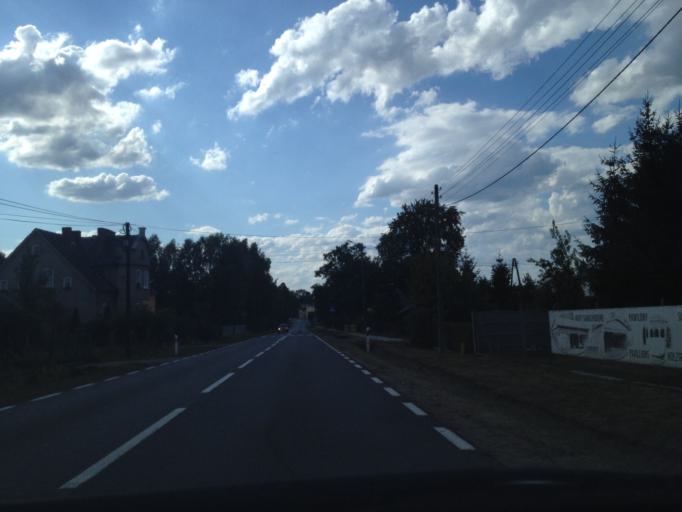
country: PL
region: Lubusz
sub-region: Powiat zarski
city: Lipinki Luzyckie
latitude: 51.6380
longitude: 15.0087
